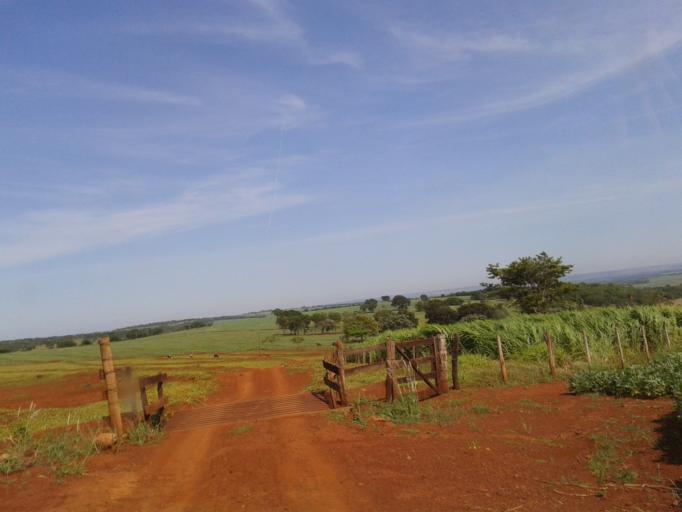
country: BR
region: Minas Gerais
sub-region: Centralina
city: Centralina
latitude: -18.7088
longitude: -49.2080
